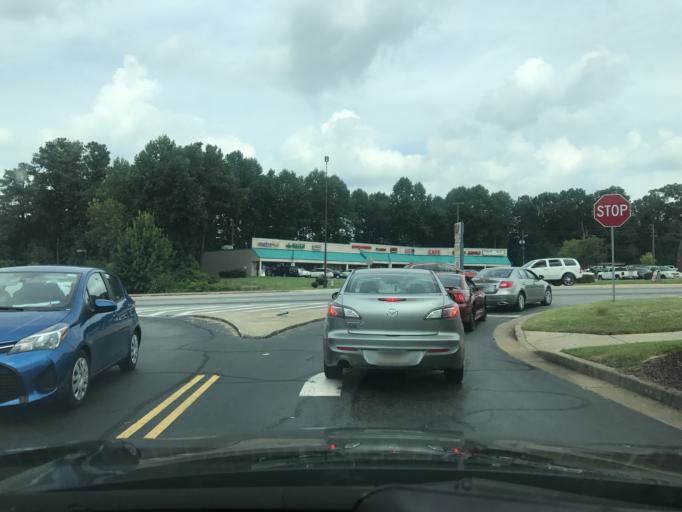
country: US
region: Georgia
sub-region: Cobb County
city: Smyrna
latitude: 33.8445
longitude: -84.5022
